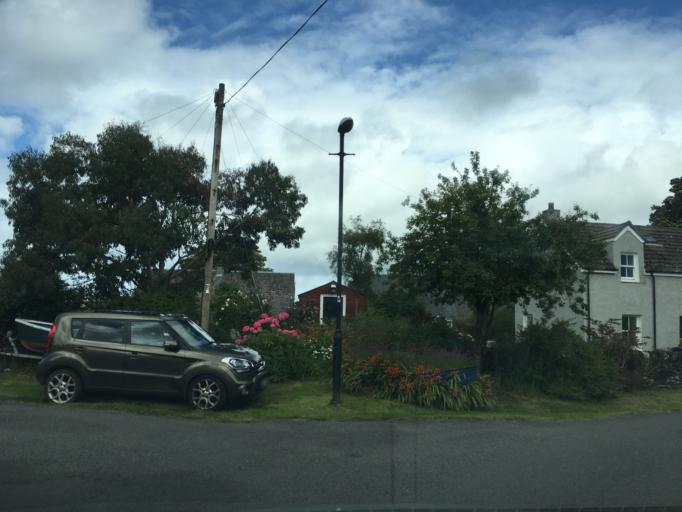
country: GB
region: Scotland
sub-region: Argyll and Bute
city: Oban
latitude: 56.2172
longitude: -5.6314
